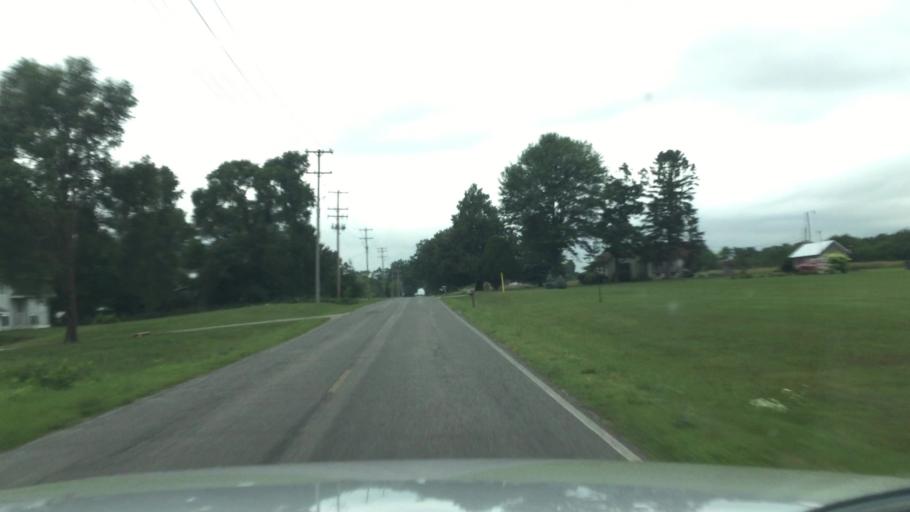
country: US
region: Michigan
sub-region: Montcalm County
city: Greenville
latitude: 43.1870
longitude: -85.2232
